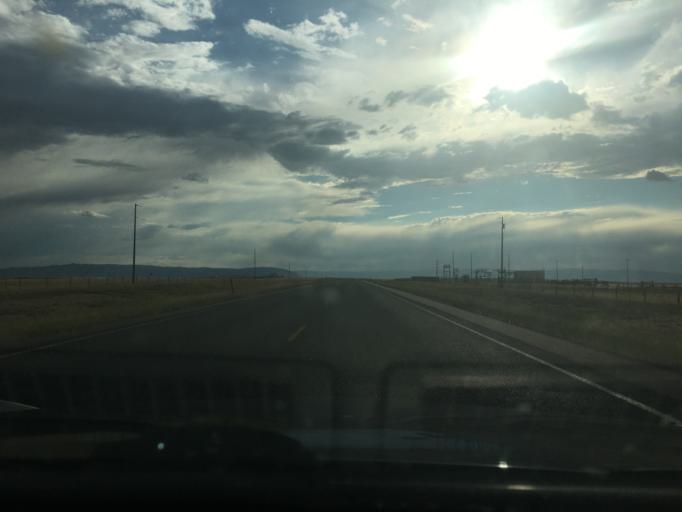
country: US
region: Wyoming
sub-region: Albany County
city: Laramie
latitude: 41.3266
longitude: -105.7234
